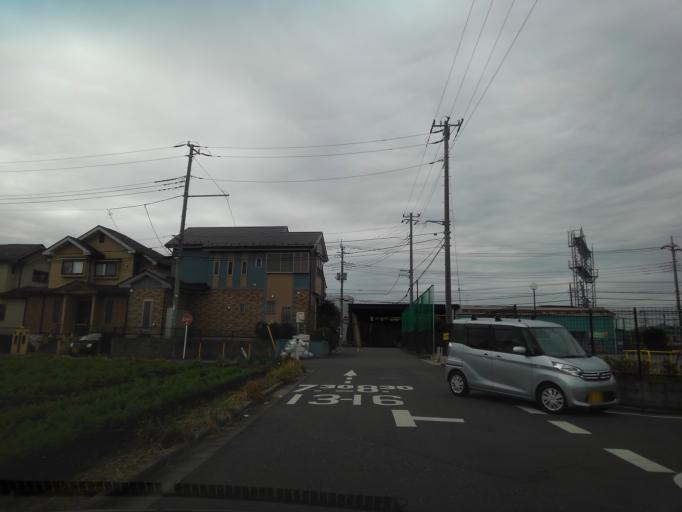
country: JP
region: Saitama
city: Tokorozawa
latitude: 35.7966
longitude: 139.4482
